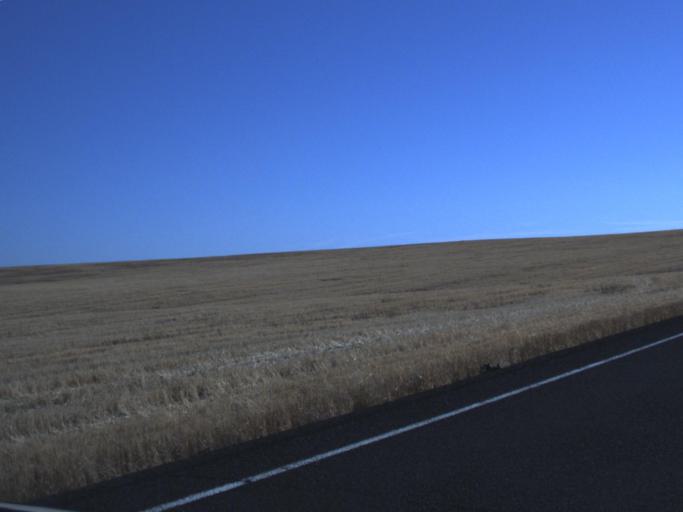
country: US
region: Washington
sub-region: Franklin County
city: Connell
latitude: 46.7632
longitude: -118.5476
